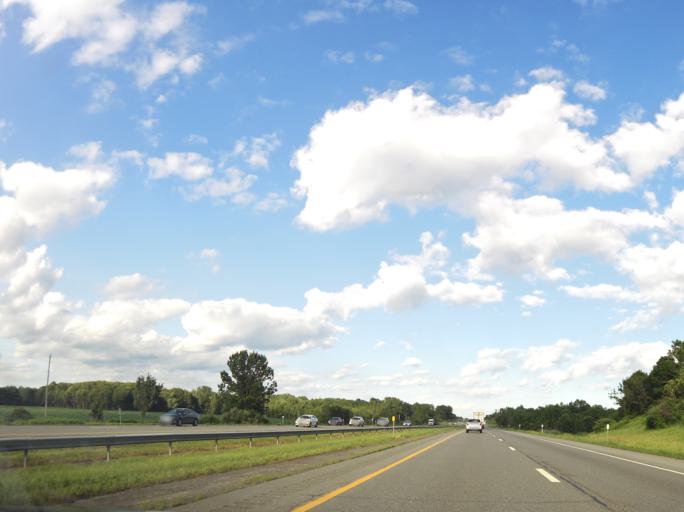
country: US
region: New York
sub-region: Genesee County
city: Oakfield
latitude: 43.0137
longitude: -78.3127
